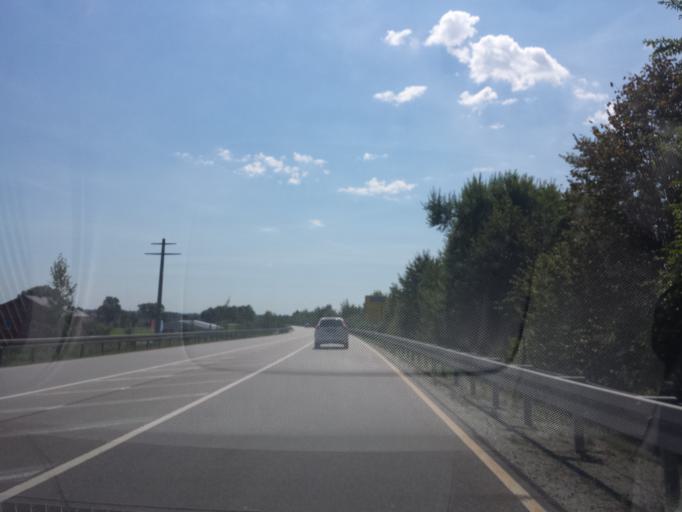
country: DE
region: Bavaria
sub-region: Lower Bavaria
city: Steinach
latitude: 48.9641
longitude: 12.6235
